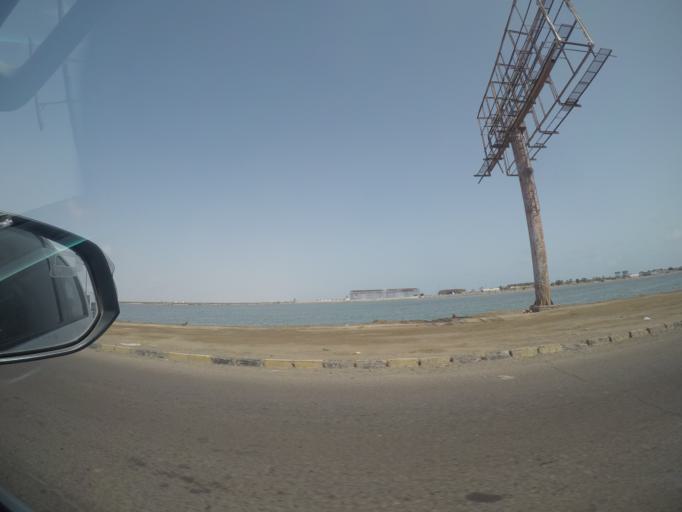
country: YE
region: Aden
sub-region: Khur Maksar
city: Khawr Maksar
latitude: 12.8217
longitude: 45.0359
